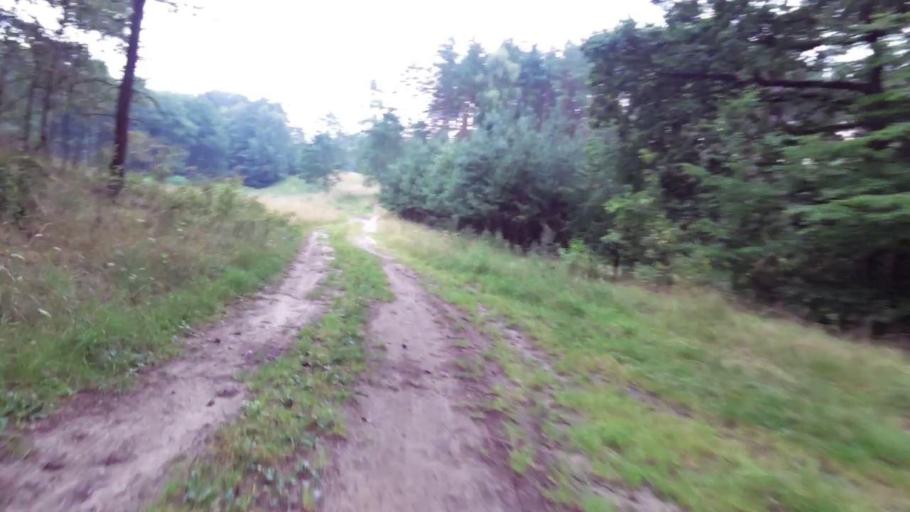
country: PL
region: West Pomeranian Voivodeship
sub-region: Powiat szczecinecki
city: Lubowo
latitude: 53.5983
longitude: 16.3848
